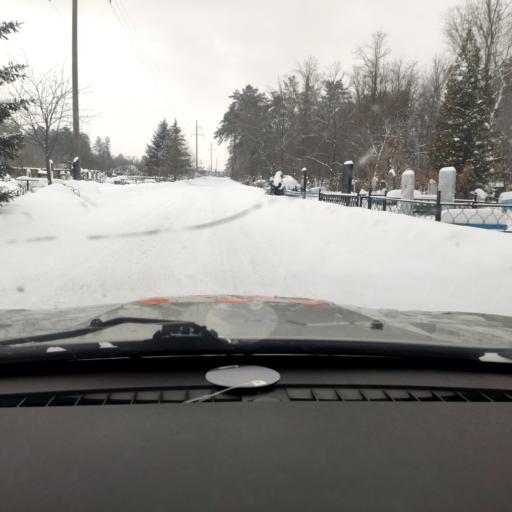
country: RU
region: Samara
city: Tol'yatti
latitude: 53.5054
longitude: 49.4551
